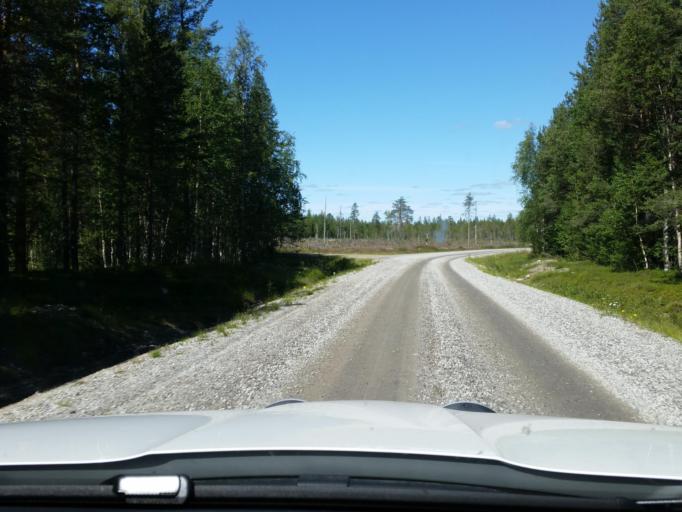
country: SE
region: Vaesterbotten
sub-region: Skelleftea Kommun
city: Storvik
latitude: 65.2684
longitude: 20.6795
